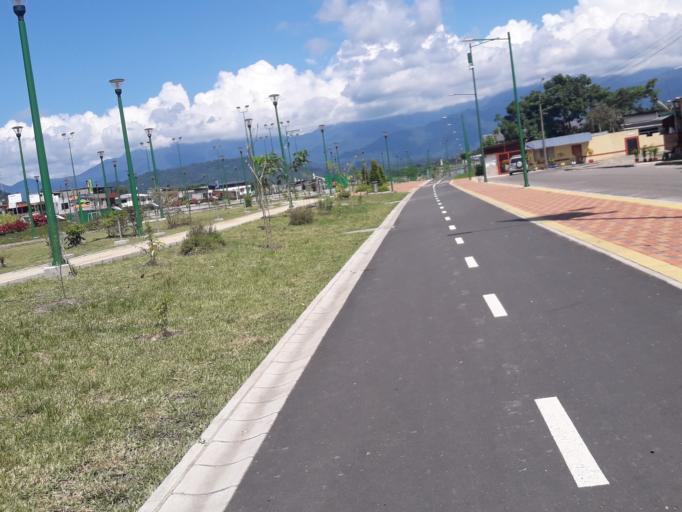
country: EC
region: Napo
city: Tena
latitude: -0.9868
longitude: -77.8171
